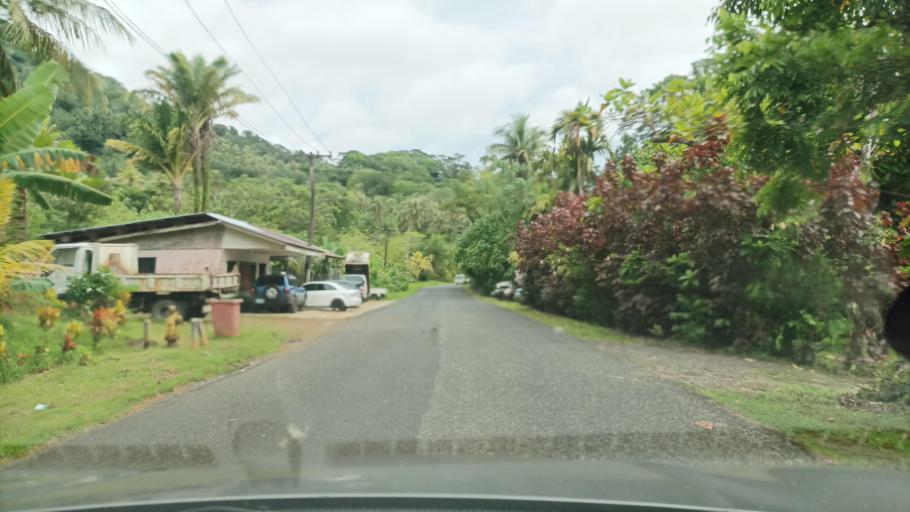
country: FM
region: Pohnpei
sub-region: Kolonia Municipality
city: Kolonia
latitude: 6.9540
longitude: 158.2438
